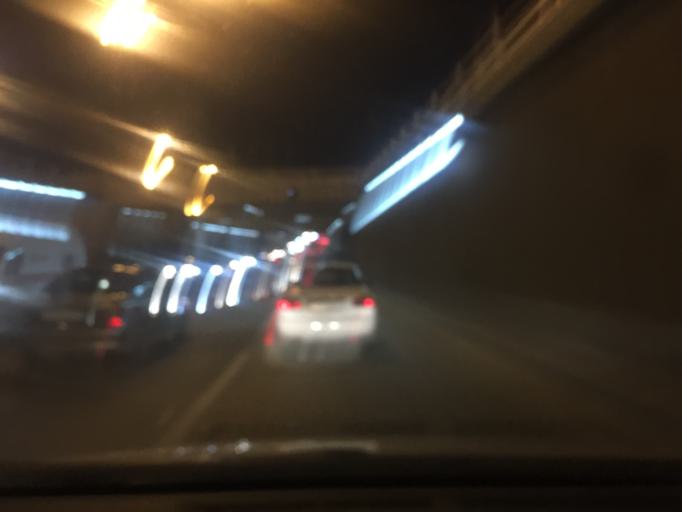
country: JO
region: Amman
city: Amman
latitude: 31.9738
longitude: 35.9105
